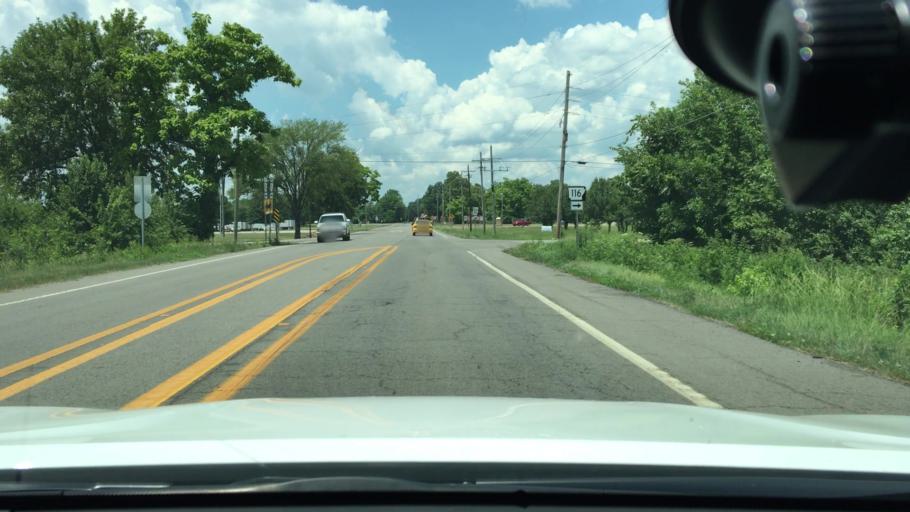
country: US
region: Arkansas
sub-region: Logan County
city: Booneville
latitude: 35.1480
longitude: -93.8766
